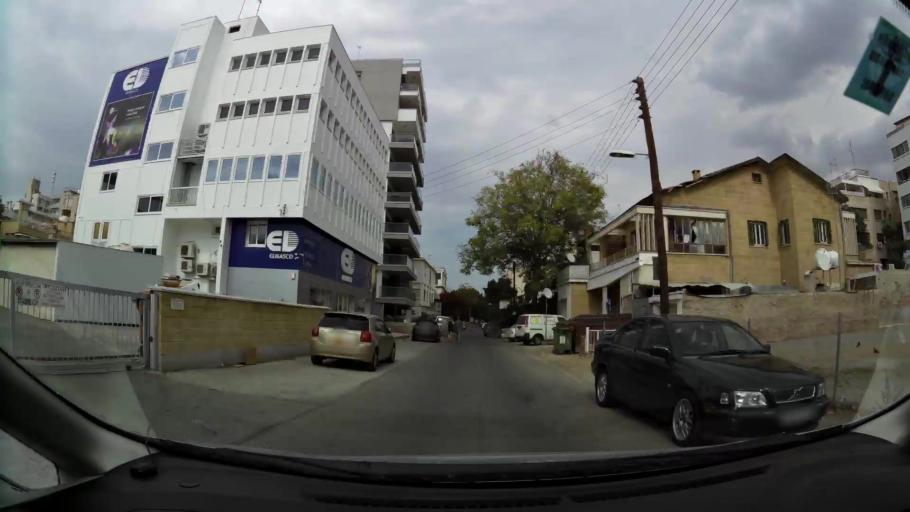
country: CY
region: Lefkosia
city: Nicosia
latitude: 35.1670
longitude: 33.3662
